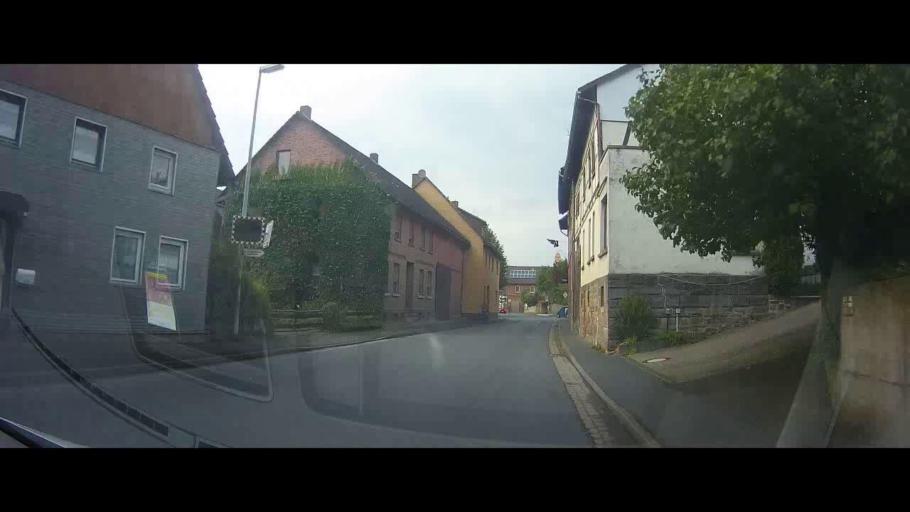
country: DE
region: Lower Saxony
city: Uslar
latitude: 51.5982
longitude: 9.6754
